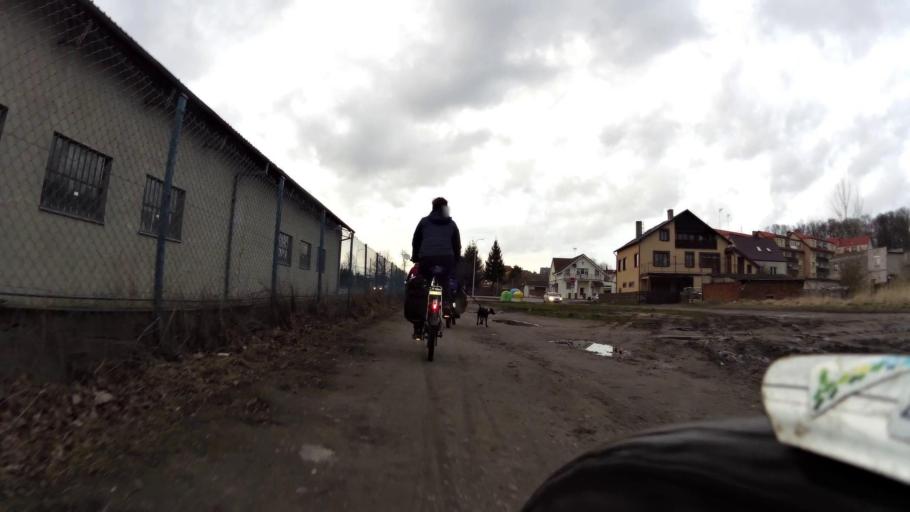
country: PL
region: West Pomeranian Voivodeship
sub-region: Powiat kamienski
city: Kamien Pomorski
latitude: 53.9672
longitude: 14.7657
